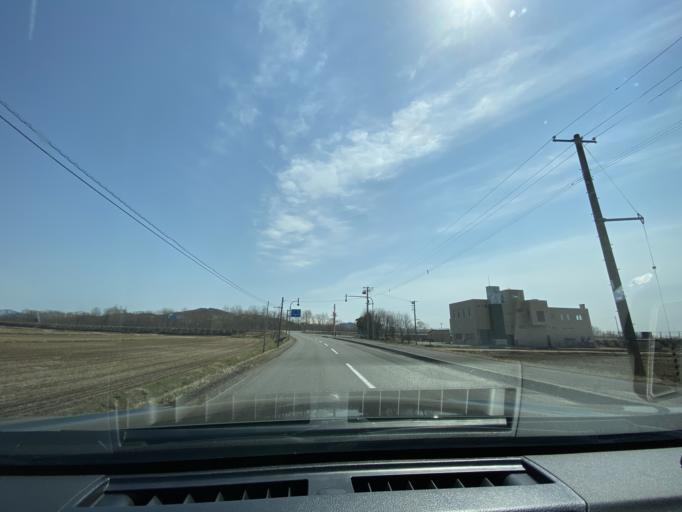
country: JP
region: Hokkaido
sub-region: Asahikawa-shi
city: Asahikawa
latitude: 43.8979
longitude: 142.5246
